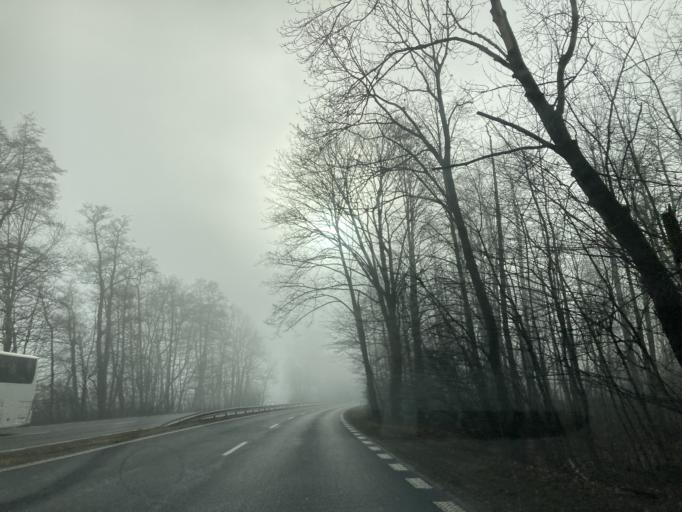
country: PL
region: Silesian Voivodeship
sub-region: Powiat cieszynski
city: Gorki Wielkie
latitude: 49.7647
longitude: 18.8093
